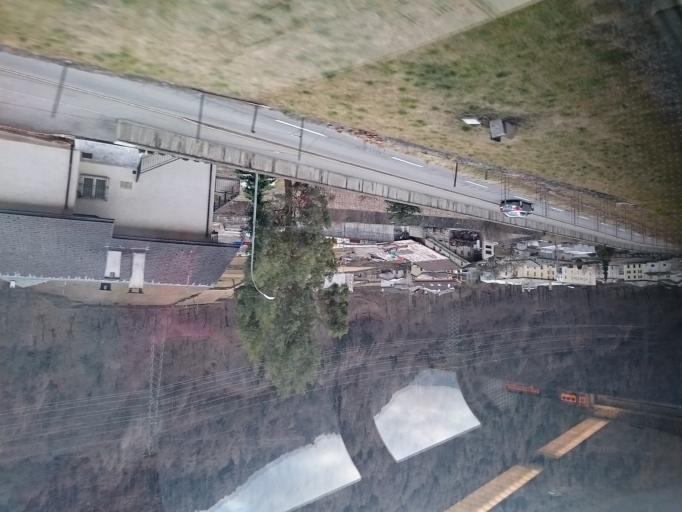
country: CH
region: Grisons
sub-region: Bernina District
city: Brusio
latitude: 46.2439
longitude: 10.1317
